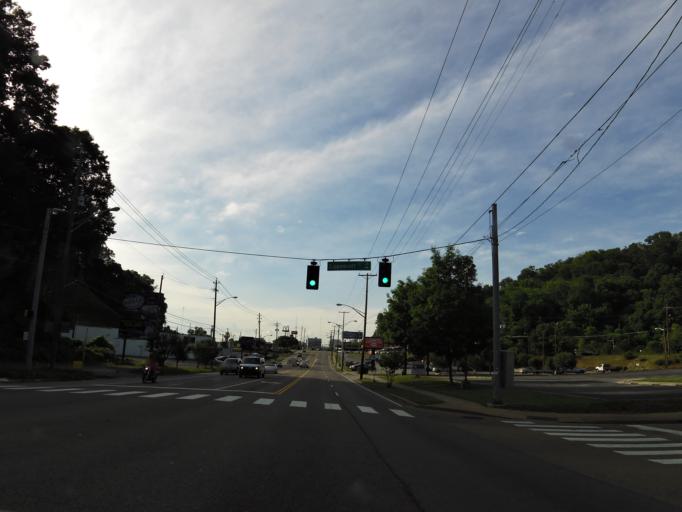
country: US
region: Tennessee
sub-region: Knox County
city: Knoxville
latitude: 35.9482
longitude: -83.9131
